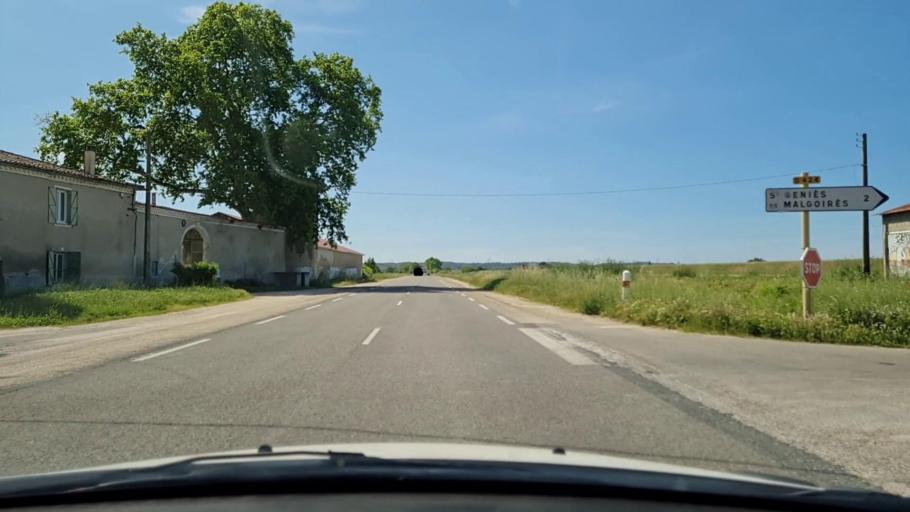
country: FR
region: Languedoc-Roussillon
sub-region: Departement du Gard
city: Saint-Genies-de-Malgoires
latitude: 43.9516
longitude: 4.2472
